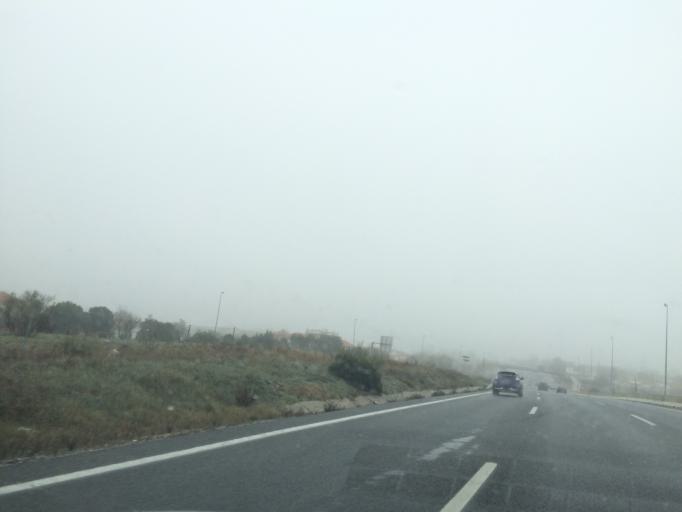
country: ES
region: Madrid
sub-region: Provincia de Madrid
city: Tres Cantos
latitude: 40.5590
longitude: -3.7127
